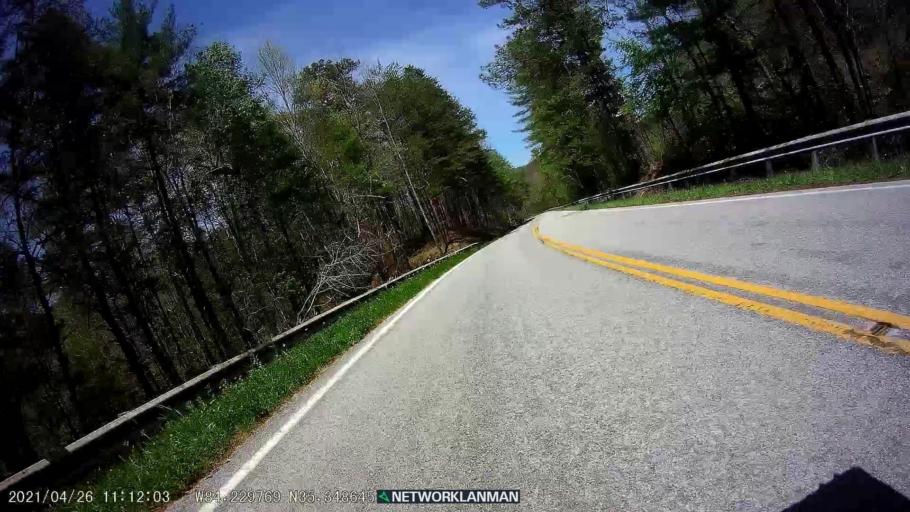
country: US
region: Tennessee
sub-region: Monroe County
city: Madisonville
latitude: 35.3483
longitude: -84.2297
